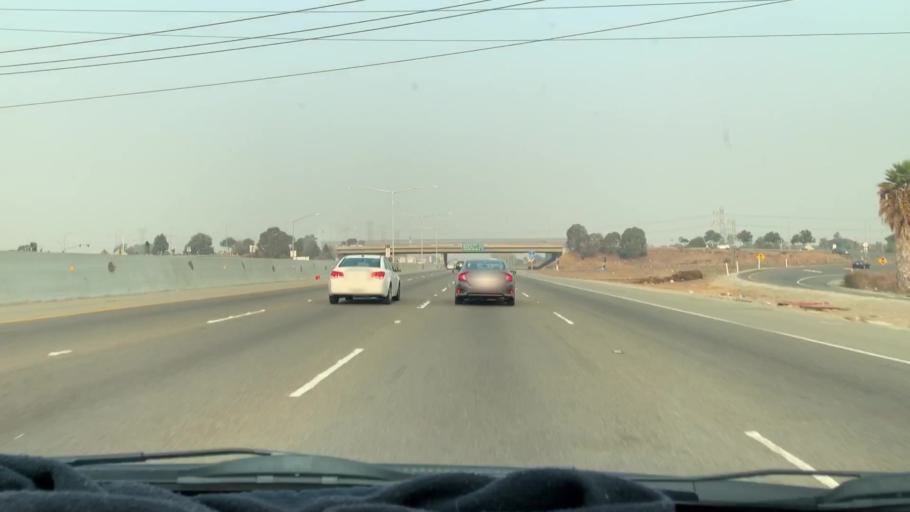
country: US
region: California
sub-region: Alameda County
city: Fremont
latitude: 37.5057
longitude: -121.9651
